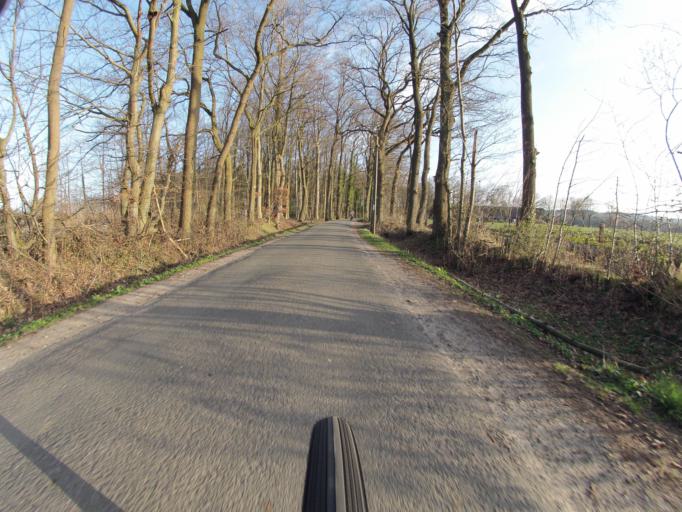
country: DE
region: North Rhine-Westphalia
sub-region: Regierungsbezirk Munster
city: Tecklenburg
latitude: 52.2511
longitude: 7.7733
